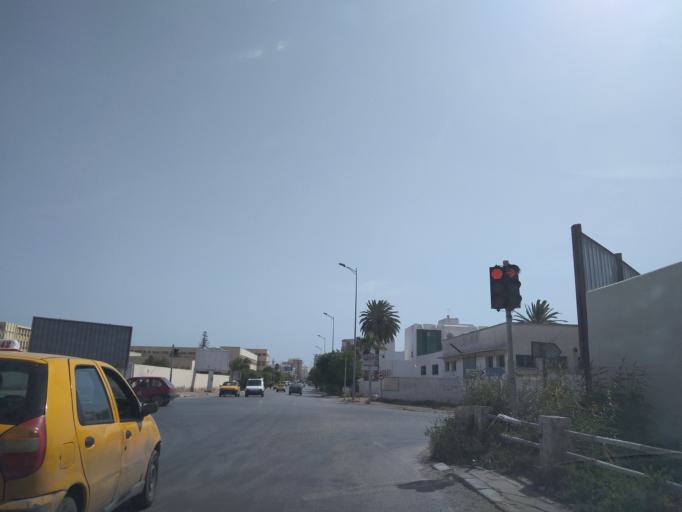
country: TN
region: Safaqis
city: Sfax
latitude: 34.7305
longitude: 10.7470
